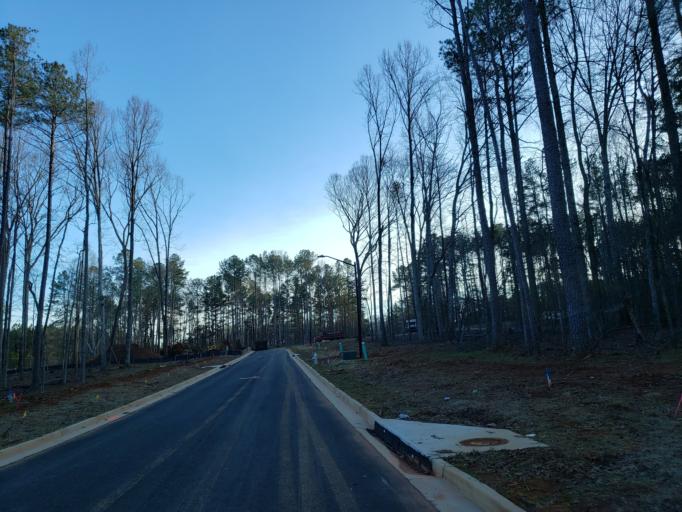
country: US
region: Georgia
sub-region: Cobb County
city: Acworth
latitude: 34.0282
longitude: -84.7310
